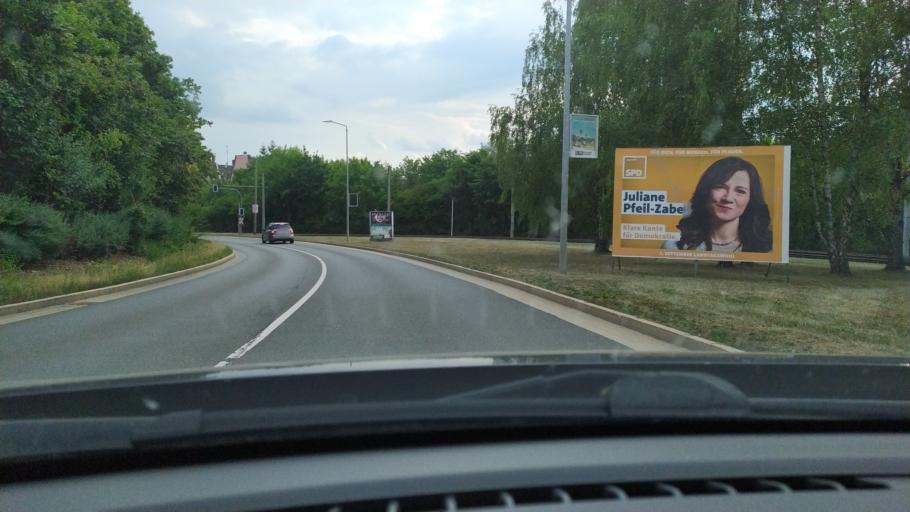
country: DE
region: Saxony
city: Plauen
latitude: 50.4963
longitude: 12.1538
